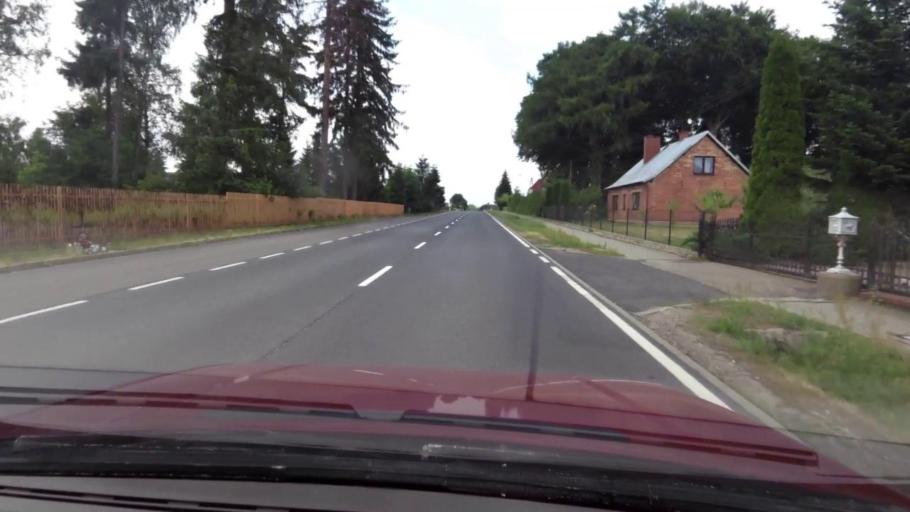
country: PL
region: Pomeranian Voivodeship
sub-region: Powiat bytowski
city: Trzebielino
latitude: 54.2439
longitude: 17.0969
